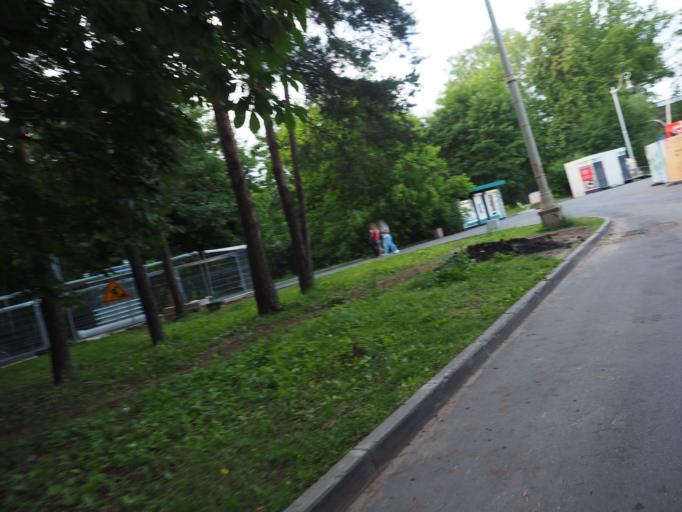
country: RU
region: Moscow
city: Ostankinskiy
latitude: 55.8404
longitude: 37.6239
